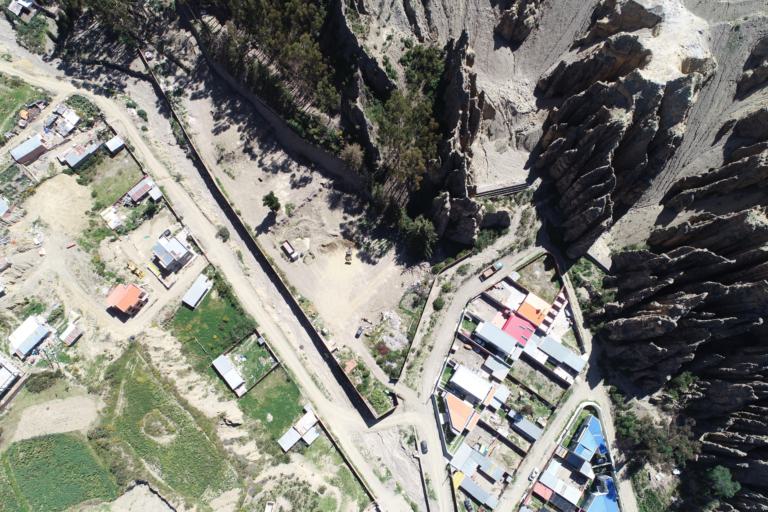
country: BO
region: La Paz
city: La Paz
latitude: -16.5087
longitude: -68.0577
